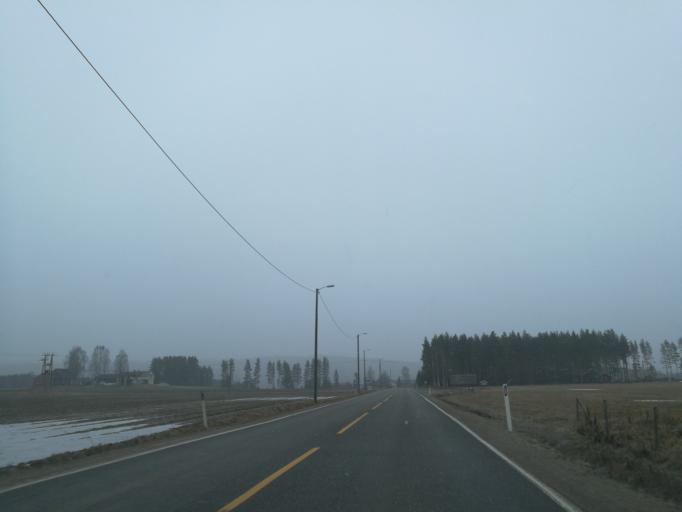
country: NO
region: Hedmark
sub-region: Asnes
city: Flisa
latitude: 60.6766
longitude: 12.1035
